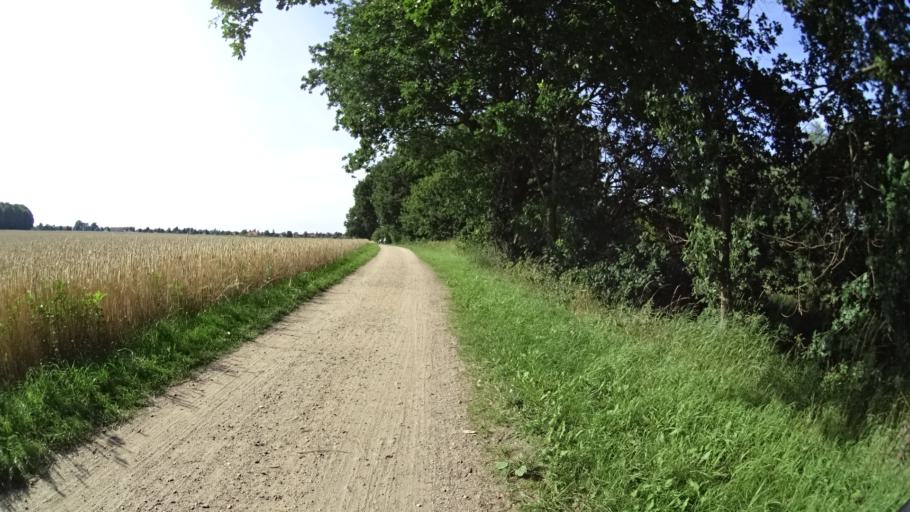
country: DE
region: Lower Saxony
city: Bardowick
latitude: 53.2841
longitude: 10.4050
